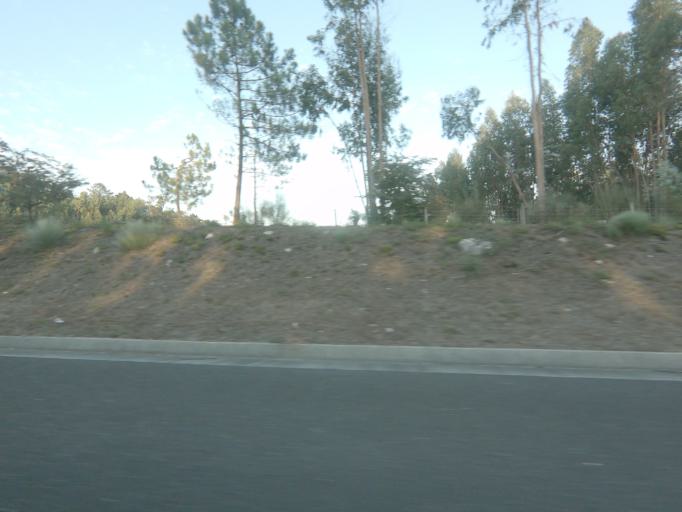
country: PT
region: Leiria
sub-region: Leiria
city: Santa Catarina da Serra
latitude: 39.6552
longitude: -8.6959
